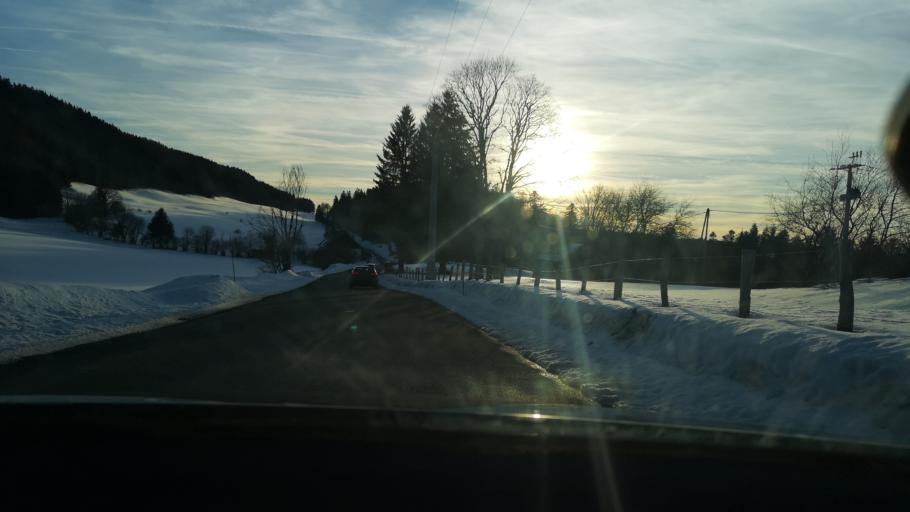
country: FR
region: Franche-Comte
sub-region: Departement du Doubs
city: Gilley
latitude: 46.9828
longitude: 6.5020
